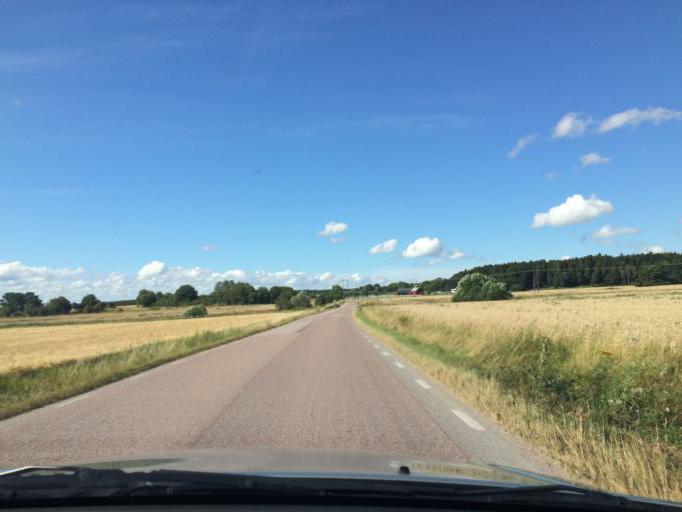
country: SE
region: Vaestmanland
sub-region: Vasteras
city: Vasteras
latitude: 59.5505
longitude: 16.4585
